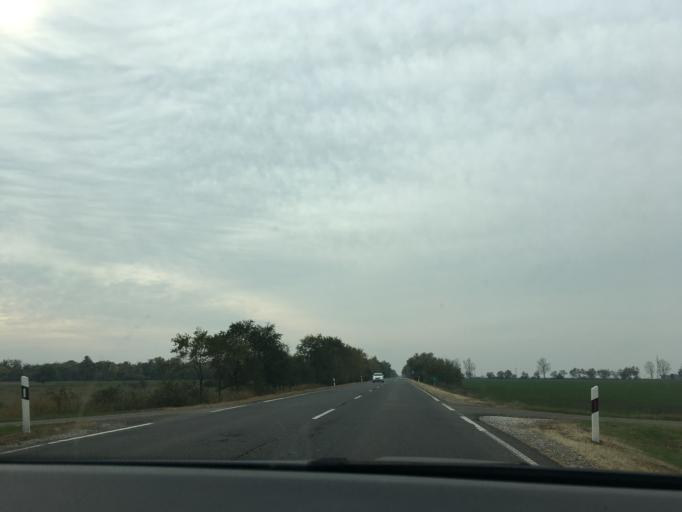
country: HU
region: Jasz-Nagykun-Szolnok
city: Karcag
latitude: 47.2835
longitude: 20.9026
